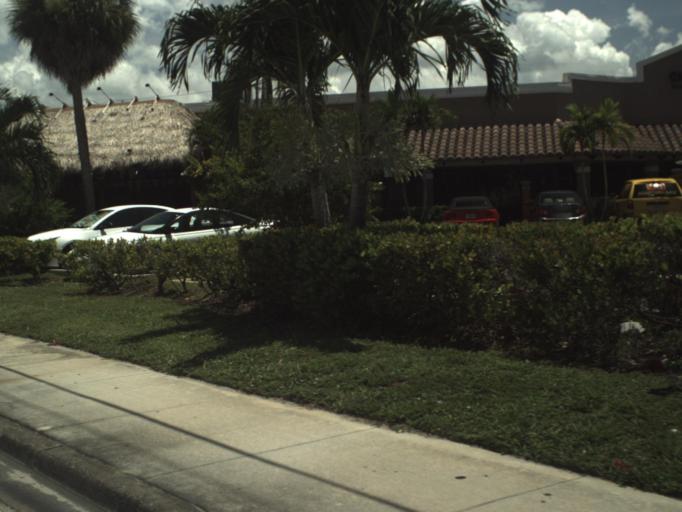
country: US
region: Florida
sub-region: Martin County
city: Stuart
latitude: 27.1836
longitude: -80.2425
